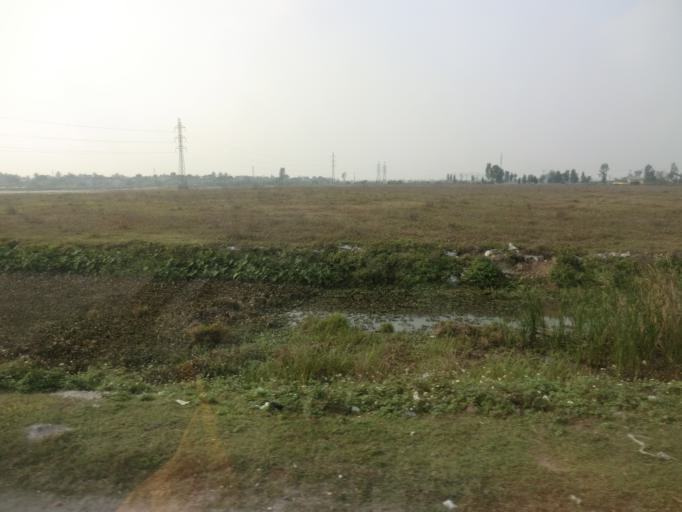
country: VN
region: Hai Duong
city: Ninh Giang
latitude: 20.6654
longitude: 106.4509
